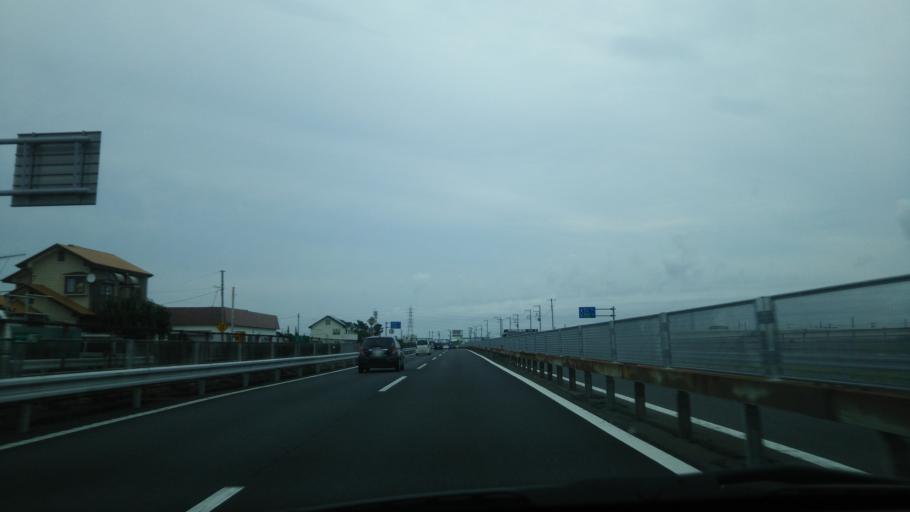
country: JP
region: Kanagawa
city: Isehara
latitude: 35.3741
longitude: 139.3197
